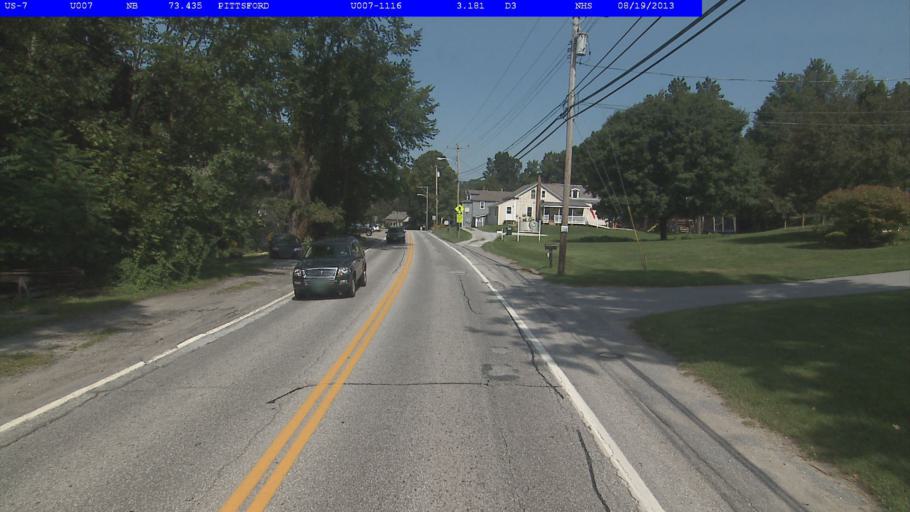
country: US
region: Vermont
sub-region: Rutland County
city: Rutland
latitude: 43.7048
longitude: -73.0135
